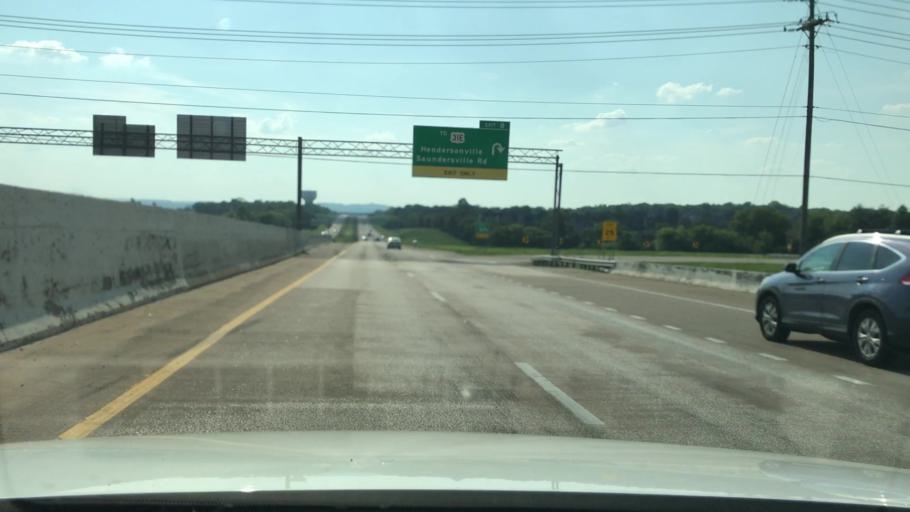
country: US
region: Tennessee
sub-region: Sumner County
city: Hendersonville
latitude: 36.3294
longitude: -86.5629
